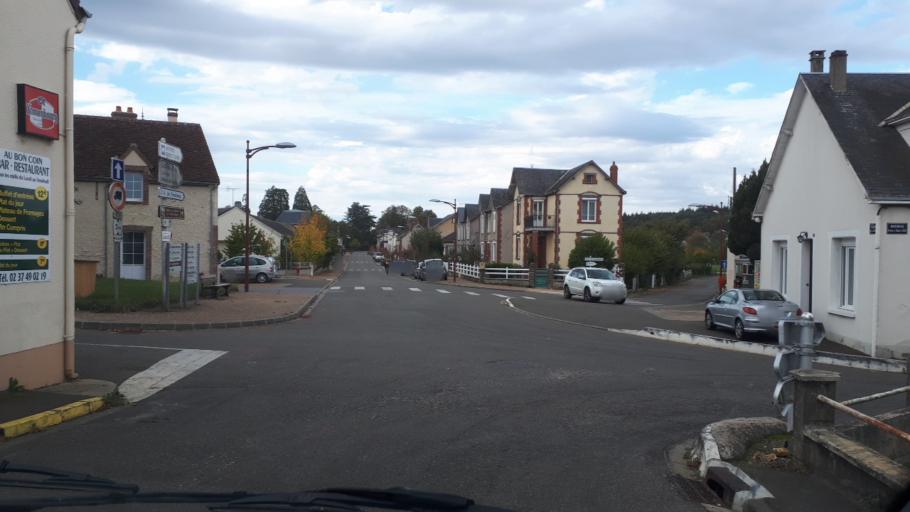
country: FR
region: Centre
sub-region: Departement d'Eure-et-Loir
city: Authon-du-Perche
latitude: 48.1970
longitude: 0.8935
